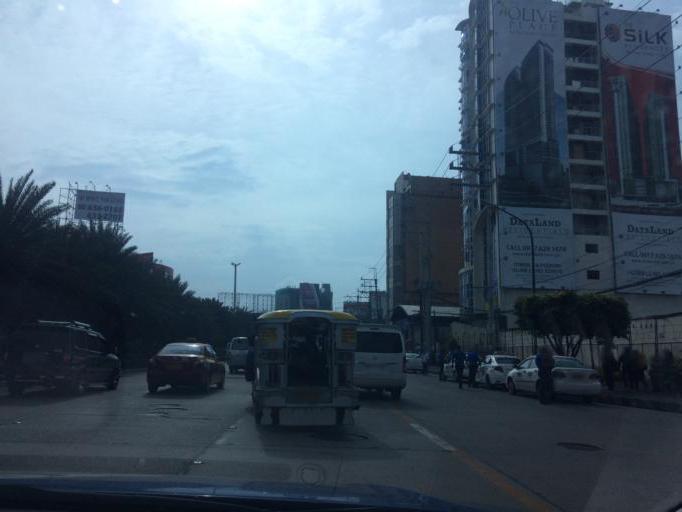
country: PH
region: Metro Manila
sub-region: Makati City
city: Makati City
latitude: 14.5376
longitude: 120.9982
